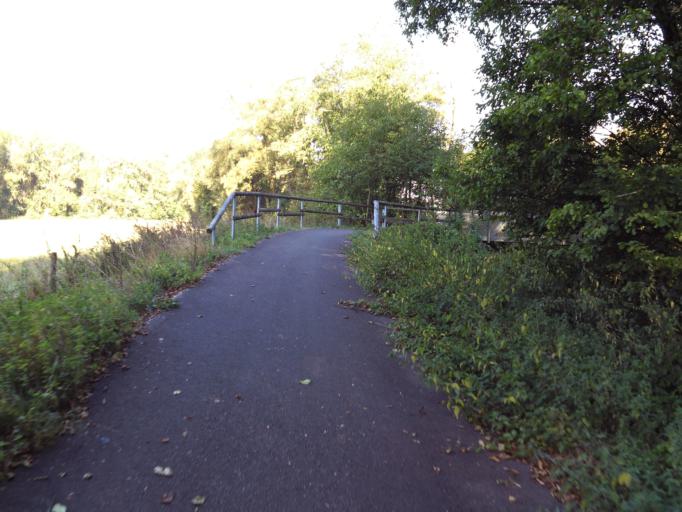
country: DE
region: Rheinland-Pfalz
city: Halsdorf
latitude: 49.9329
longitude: 6.3525
